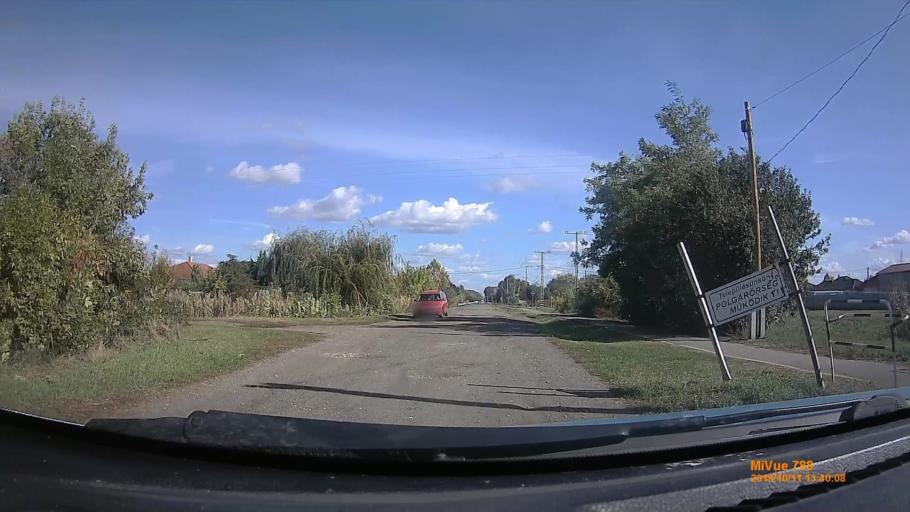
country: HU
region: Hajdu-Bihar
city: Balmazujvaros
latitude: 47.5398
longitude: 21.3344
